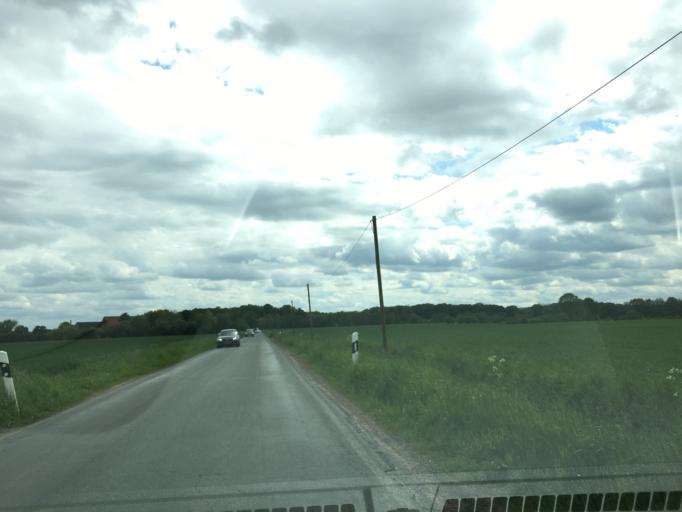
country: DE
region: North Rhine-Westphalia
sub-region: Regierungsbezirk Munster
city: Havixbeck
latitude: 51.9846
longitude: 7.4738
